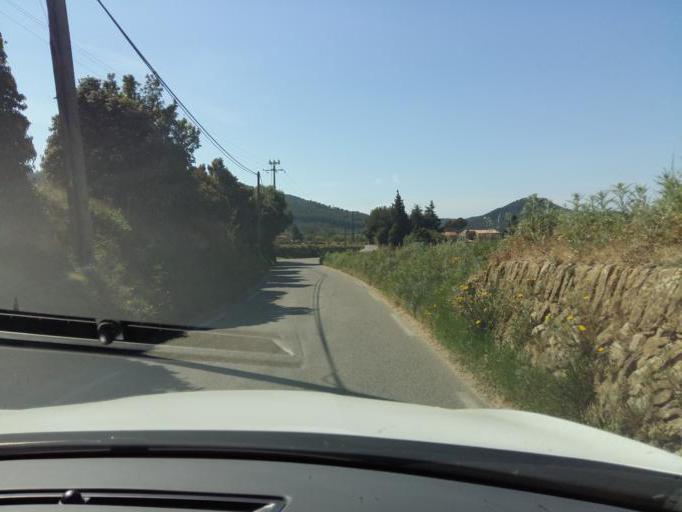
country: FR
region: Provence-Alpes-Cote d'Azur
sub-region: Departement du Var
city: Saint-Cyr-sur-Mer
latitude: 43.1805
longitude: 5.7327
